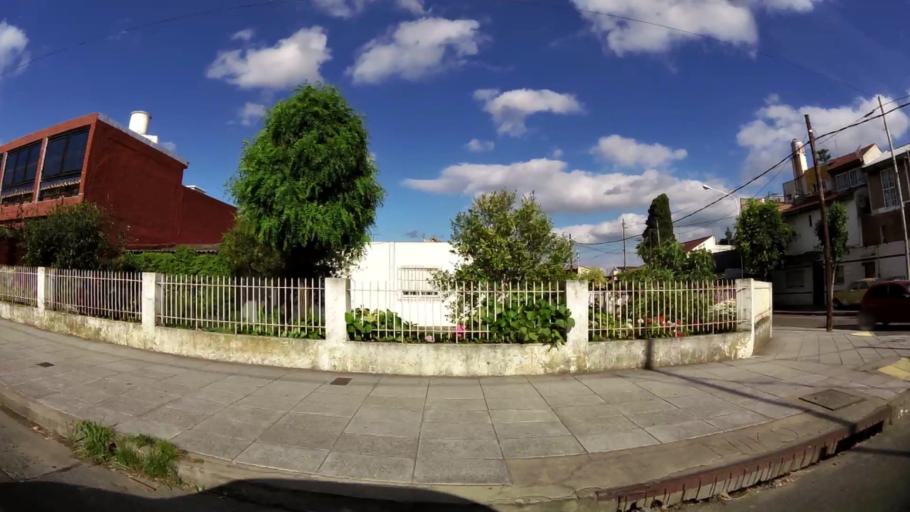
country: AR
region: Buenos Aires
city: San Justo
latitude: -34.6962
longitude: -58.5905
